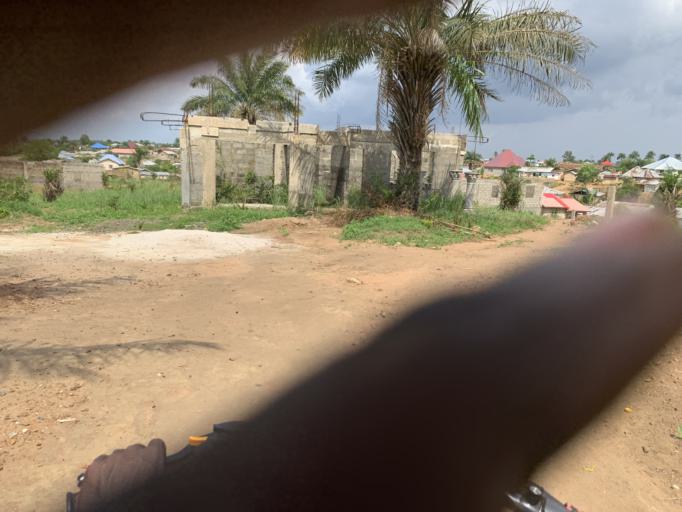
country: SL
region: Western Area
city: Waterloo
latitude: 8.3586
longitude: -13.0433
